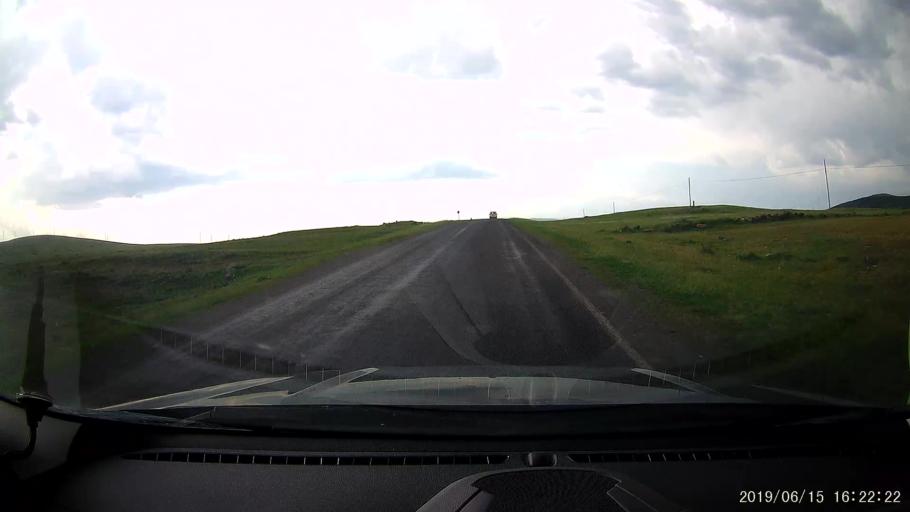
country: TR
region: Ardahan
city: Hanak
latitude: 41.1888
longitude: 42.8498
